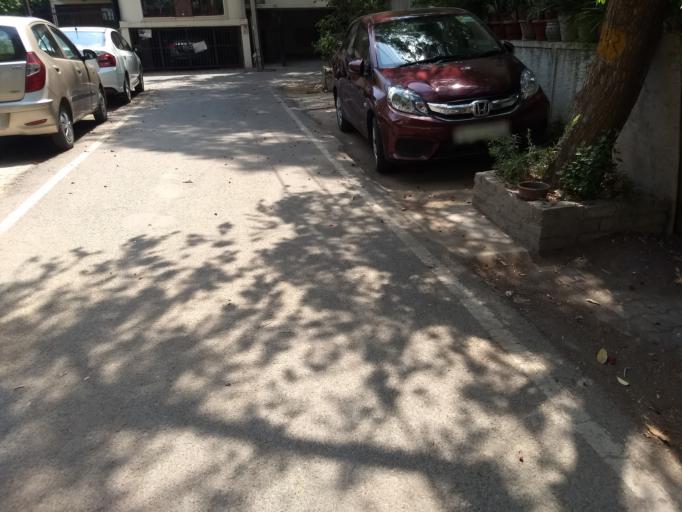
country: IN
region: NCT
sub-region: New Delhi
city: New Delhi
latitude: 28.5569
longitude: 77.2142
